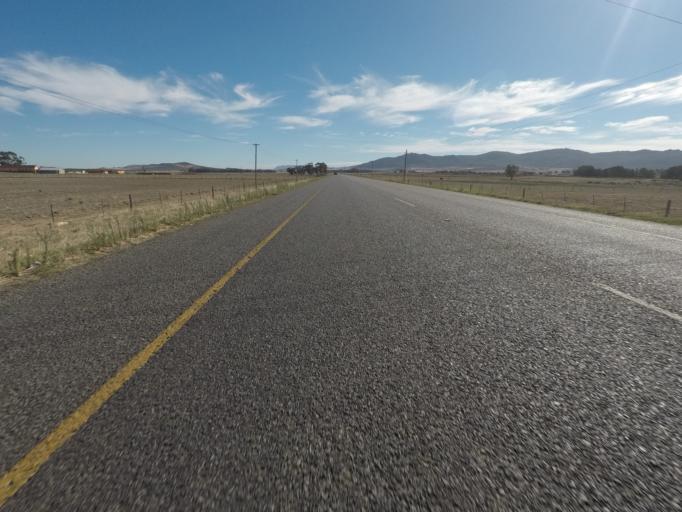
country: ZA
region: Western Cape
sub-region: West Coast District Municipality
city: Malmesbury
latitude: -33.6364
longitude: 18.7190
